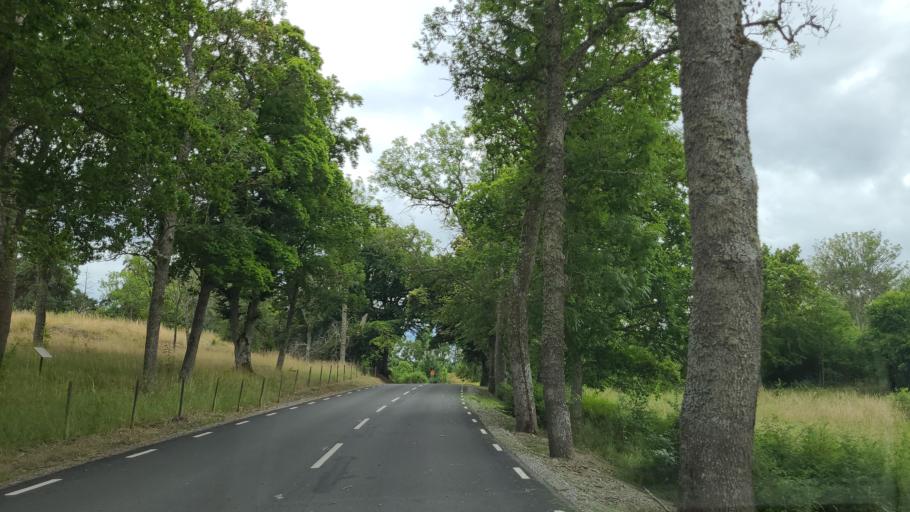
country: SE
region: Stockholm
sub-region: Upplands-Bro Kommun
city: Bro
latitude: 59.5041
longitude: 17.6250
